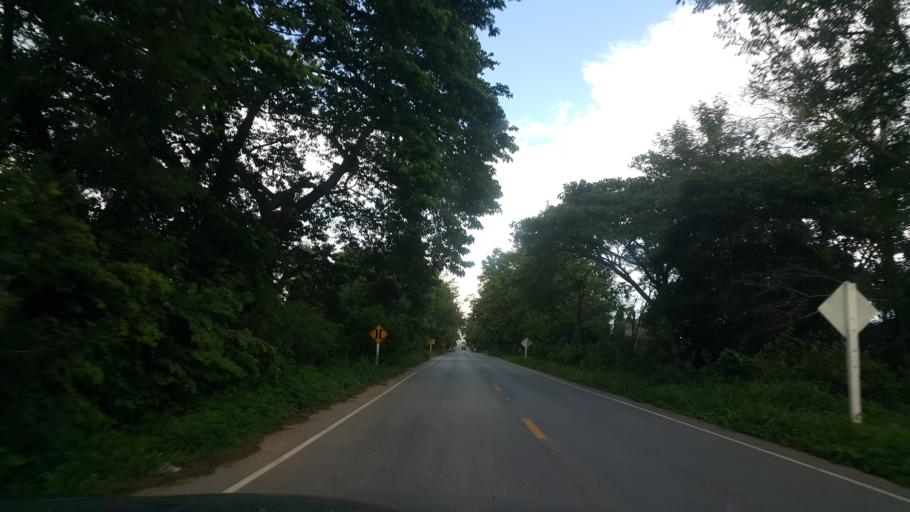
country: TH
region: Tak
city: Sam Ngao
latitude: 17.2051
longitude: 99.0970
